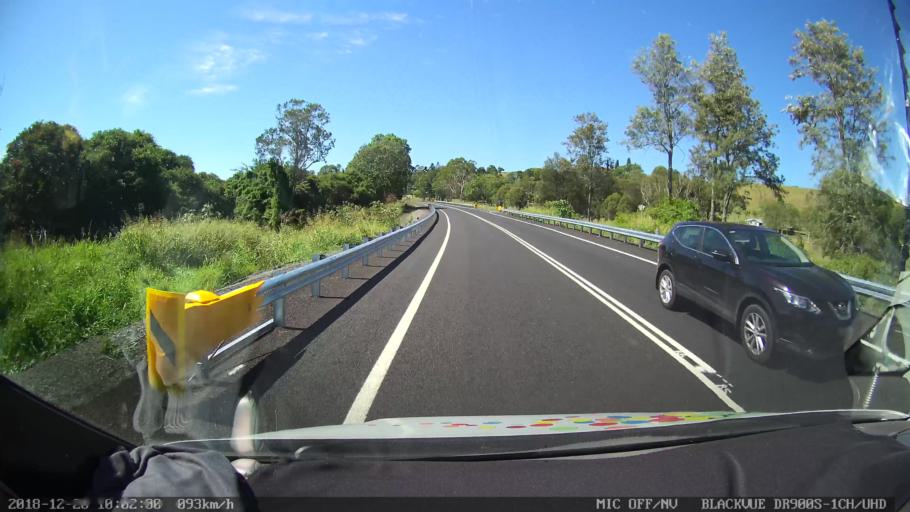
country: AU
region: New South Wales
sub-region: Lismore Municipality
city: Lismore
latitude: -28.8521
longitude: 153.2610
